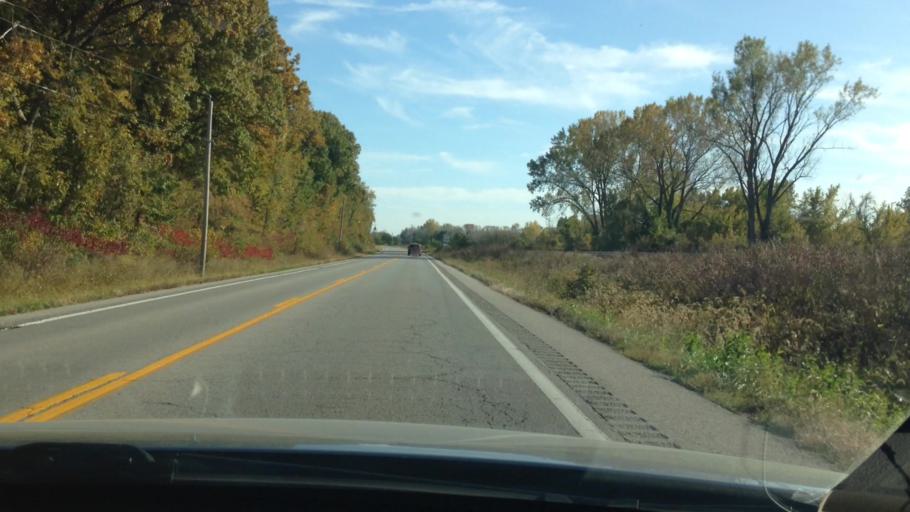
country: US
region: Kansas
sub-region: Leavenworth County
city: Leavenworth
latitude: 39.3193
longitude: -94.8539
